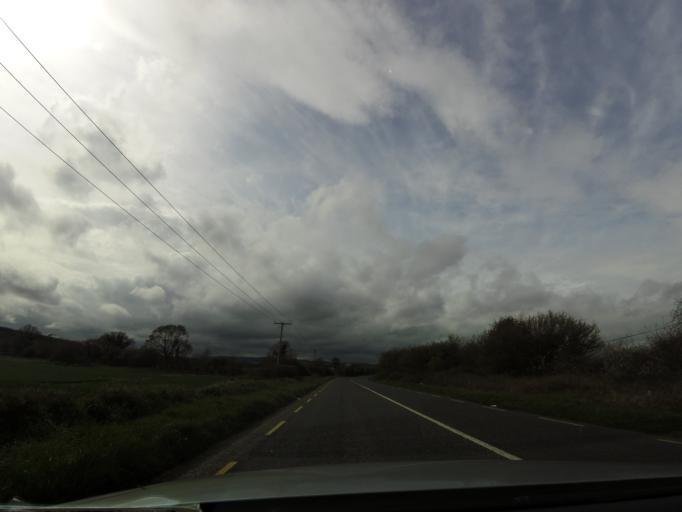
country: IE
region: Leinster
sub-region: Kilkenny
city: Ballyragget
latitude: 52.7268
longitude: -7.3743
